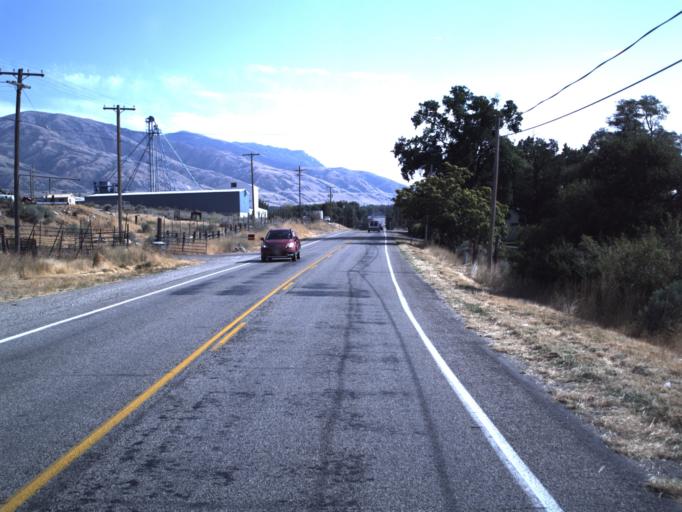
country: US
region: Utah
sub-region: Box Elder County
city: Brigham City
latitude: 41.5446
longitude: -112.0152
